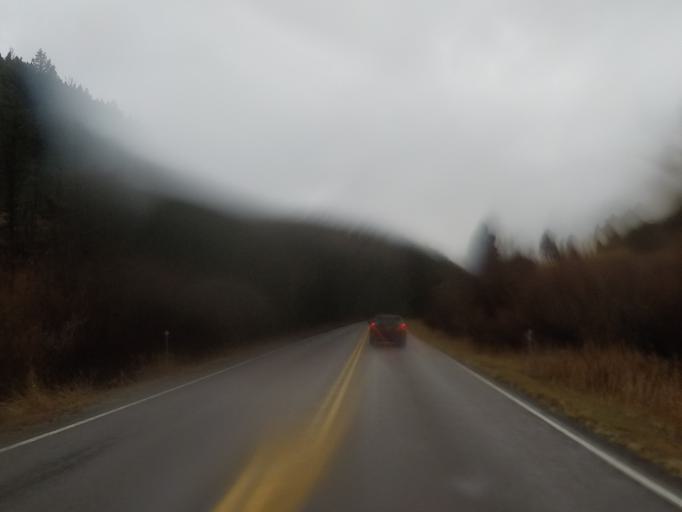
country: US
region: Montana
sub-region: Broadwater County
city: Townsend
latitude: 46.3295
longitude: -111.2030
